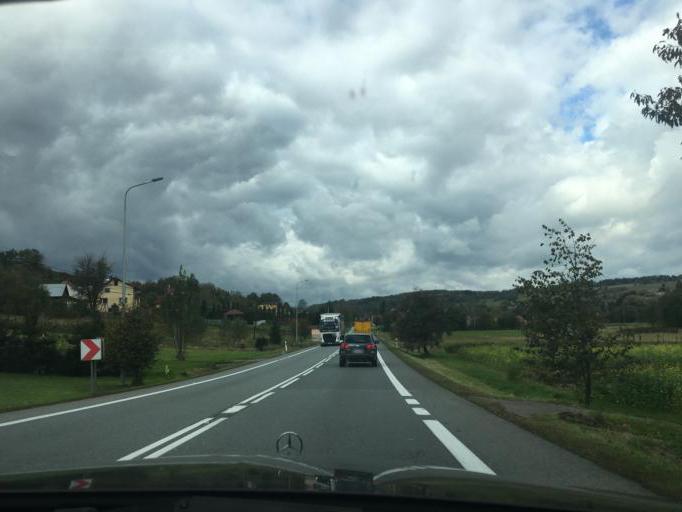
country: PL
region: Subcarpathian Voivodeship
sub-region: Powiat strzyzowski
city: Polomia
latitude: 49.8884
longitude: 21.8965
